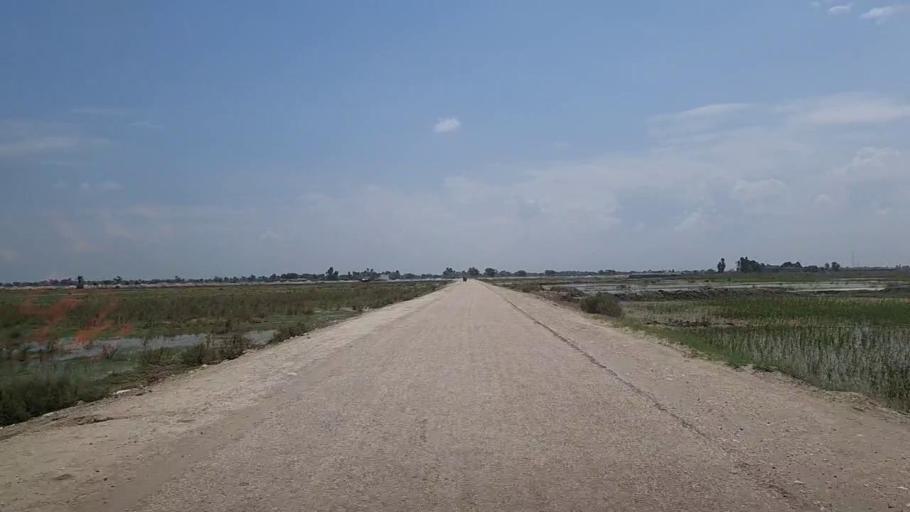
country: PK
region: Sindh
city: Kandhkot
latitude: 28.2792
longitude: 69.1743
